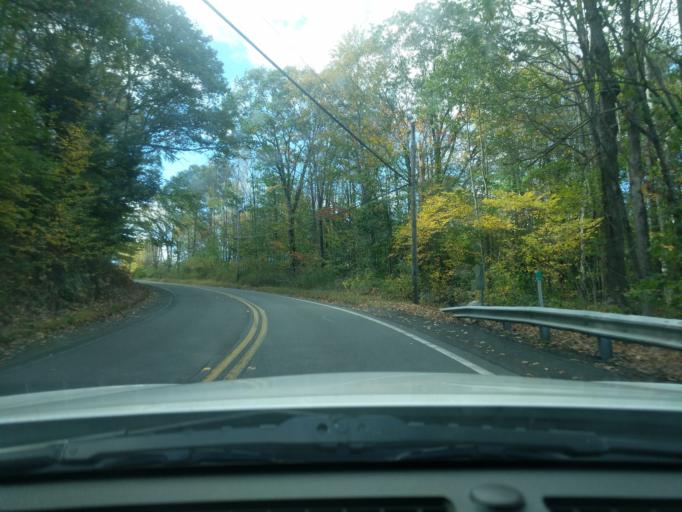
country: US
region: Massachusetts
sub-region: Berkshire County
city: Otis
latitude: 42.1747
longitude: -72.9640
